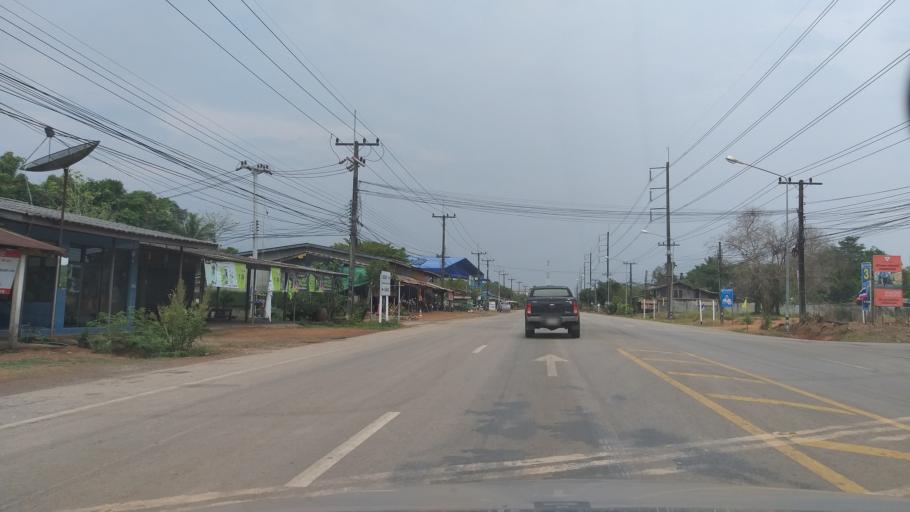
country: TH
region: Trat
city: Khao Saming
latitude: 12.3035
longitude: 102.3455
